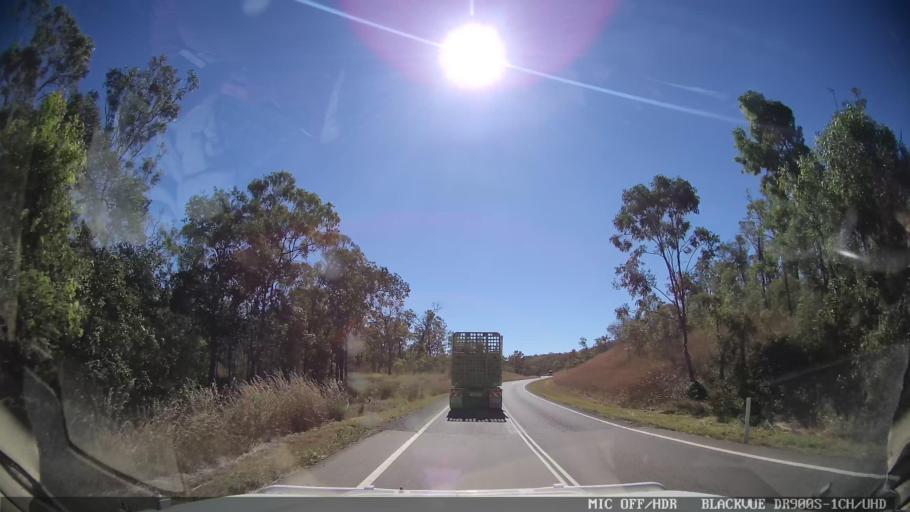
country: AU
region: Queensland
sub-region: Gladstone
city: Toolooa
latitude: -24.1545
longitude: 151.2109
